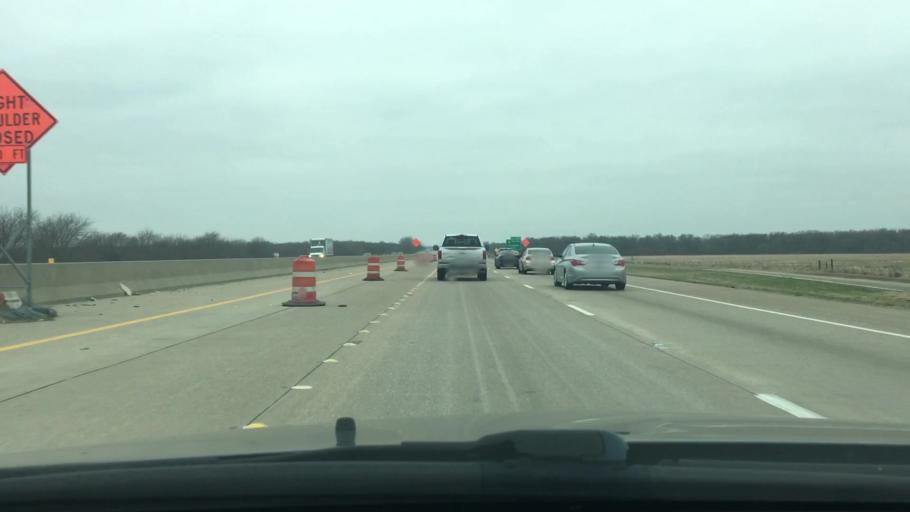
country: US
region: Texas
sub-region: Navarro County
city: Corsicana
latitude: 32.1713
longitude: -96.4703
